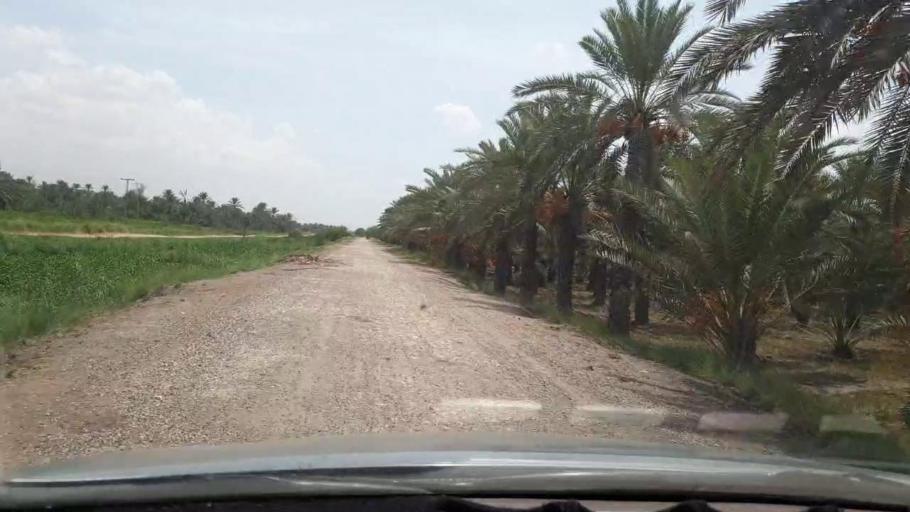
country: PK
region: Sindh
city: Khairpur
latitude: 27.4582
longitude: 68.7911
